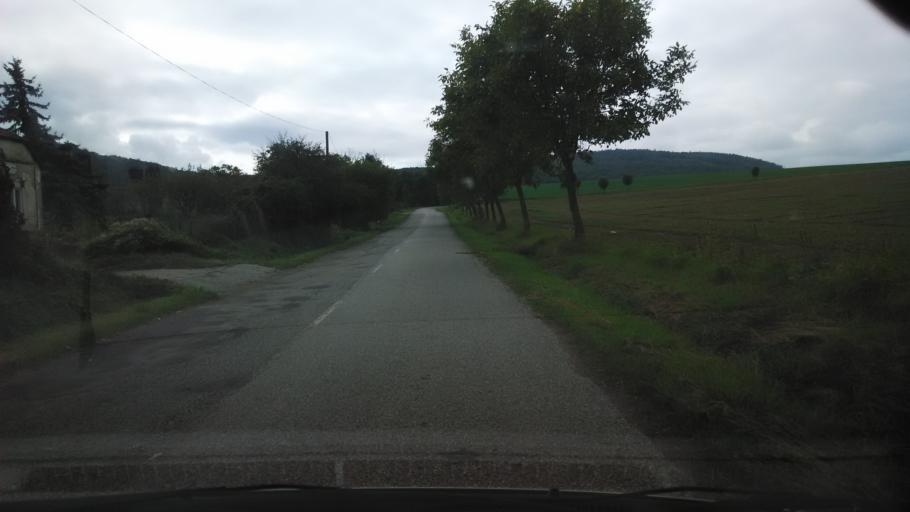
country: SK
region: Nitriansky
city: Tlmace
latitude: 48.3034
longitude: 18.4998
